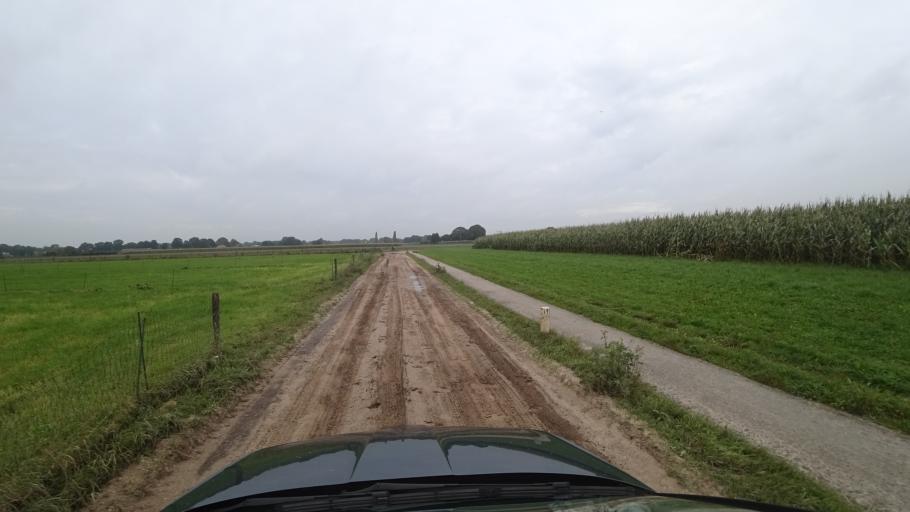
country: NL
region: Gelderland
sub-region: Gemeente Ede
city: Lunteren
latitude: 52.0652
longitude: 5.6462
